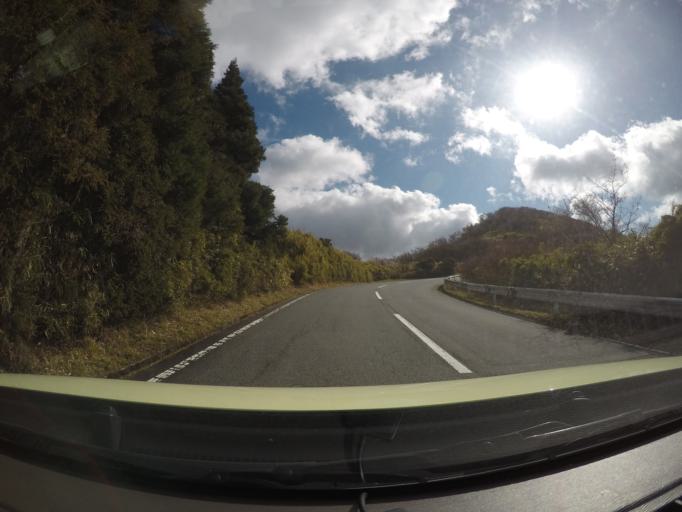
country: JP
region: Kanagawa
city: Hakone
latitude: 35.2029
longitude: 138.9876
